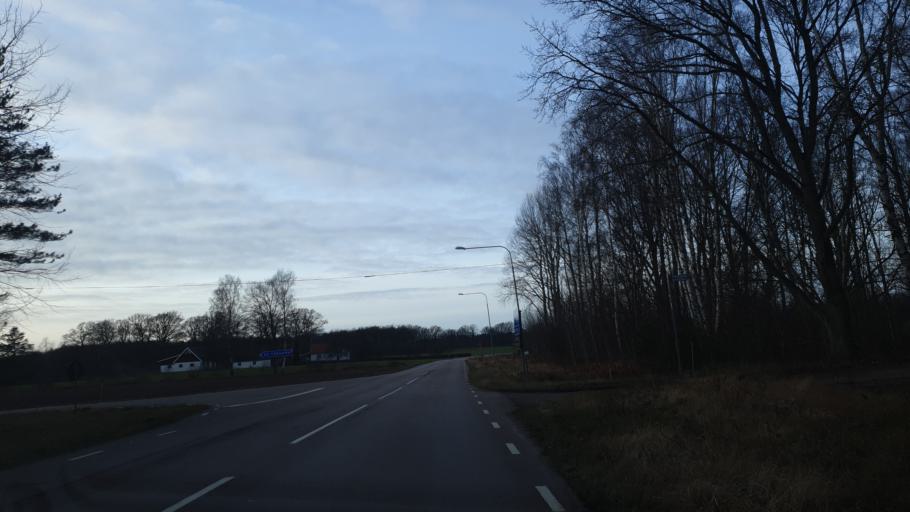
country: SE
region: Kalmar
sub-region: Torsas Kommun
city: Torsas
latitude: 56.2548
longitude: 16.0114
